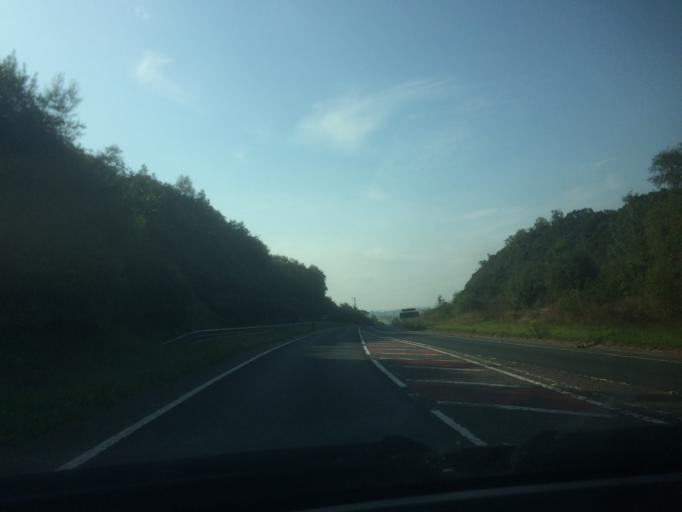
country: GB
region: England
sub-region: Cornwall
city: Pillaton
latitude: 50.4545
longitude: -4.2564
